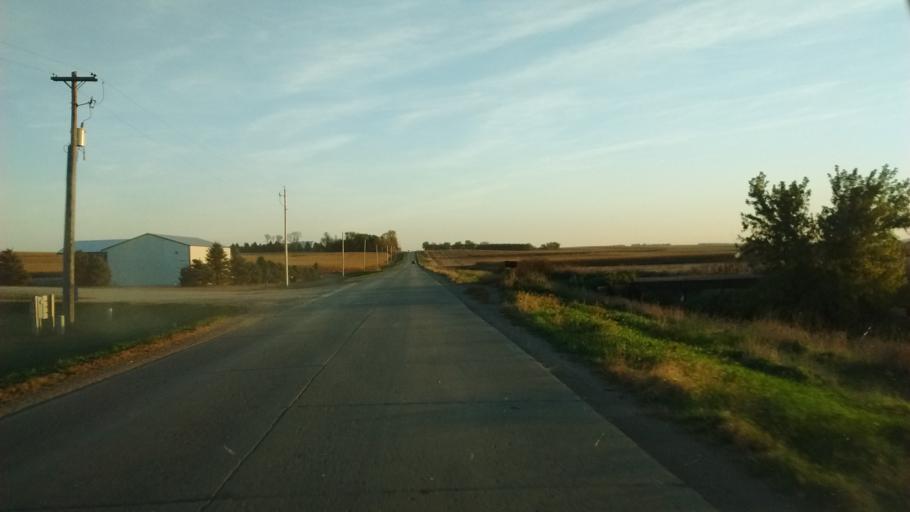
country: US
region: Iowa
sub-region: Plymouth County
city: Le Mars
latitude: 42.7589
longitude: -96.1555
